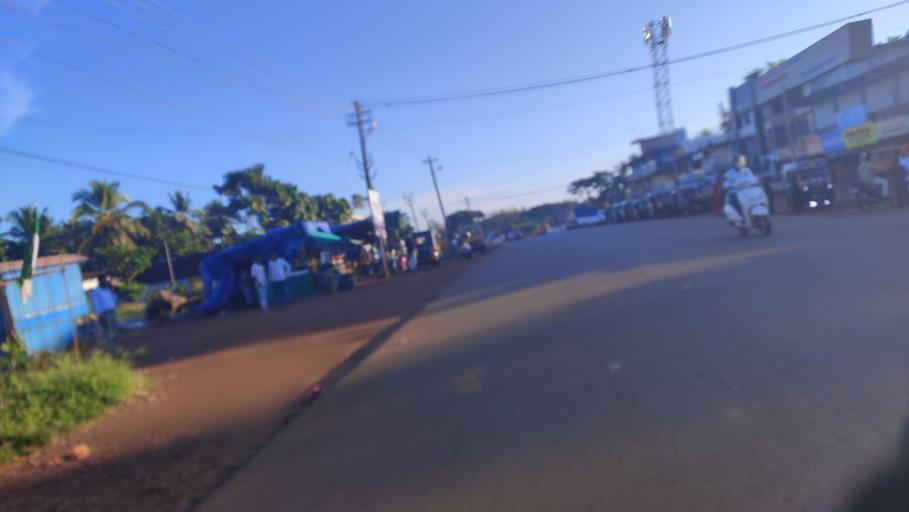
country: IN
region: Kerala
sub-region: Kasaragod District
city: Kasaragod
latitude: 12.4800
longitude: 75.0580
